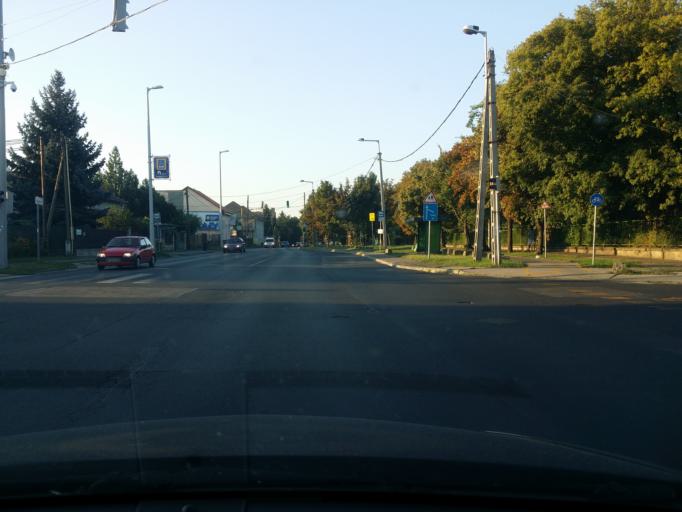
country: HU
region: Budapest
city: Budapest XVI. keruelet
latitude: 47.5030
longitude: 19.1530
